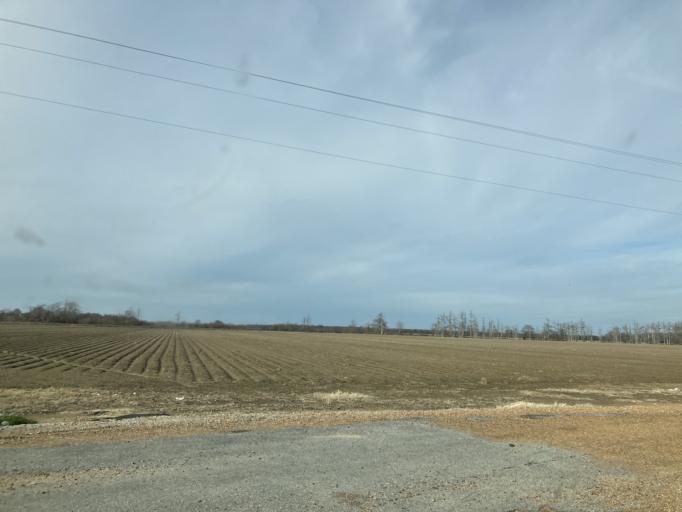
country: US
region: Mississippi
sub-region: Humphreys County
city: Belzoni
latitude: 33.0616
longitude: -90.6331
